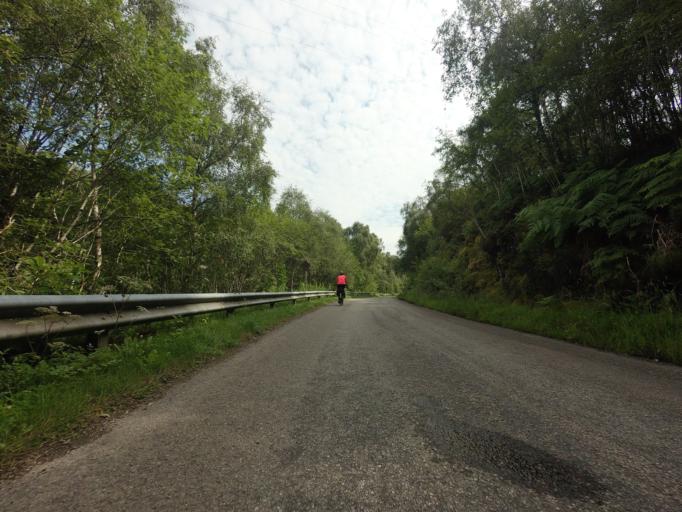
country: GB
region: Scotland
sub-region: Highland
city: Evanton
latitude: 57.9515
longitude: -4.4057
